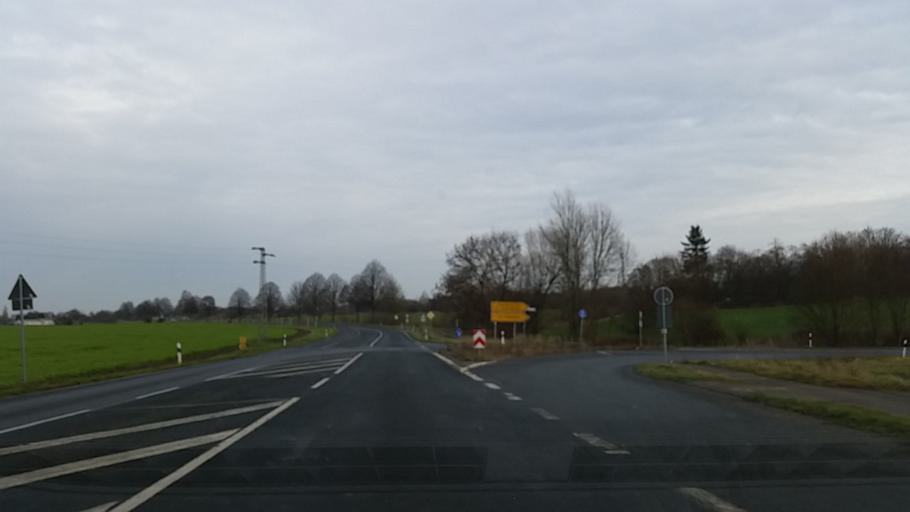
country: DE
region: Lower Saxony
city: Liebenburg
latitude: 52.0622
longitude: 10.4033
